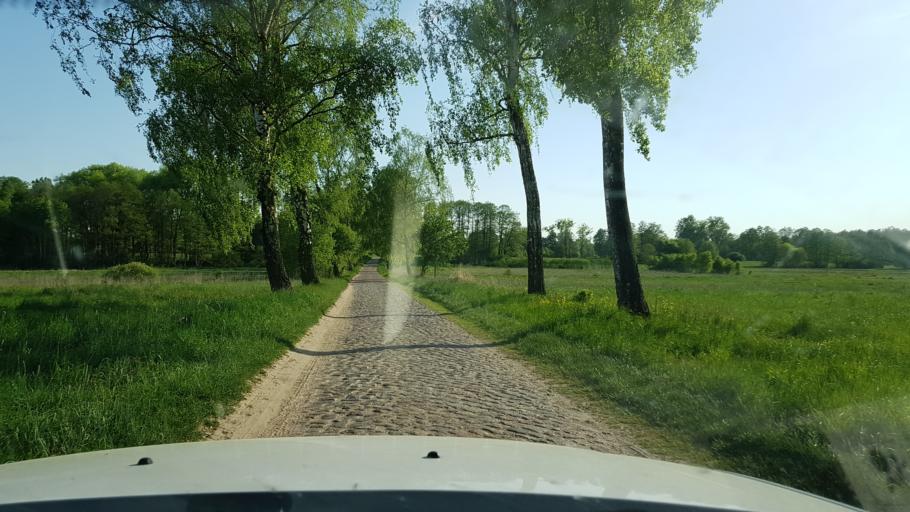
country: PL
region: West Pomeranian Voivodeship
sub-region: Powiat lobeski
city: Resko
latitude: 53.7142
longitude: 15.3379
